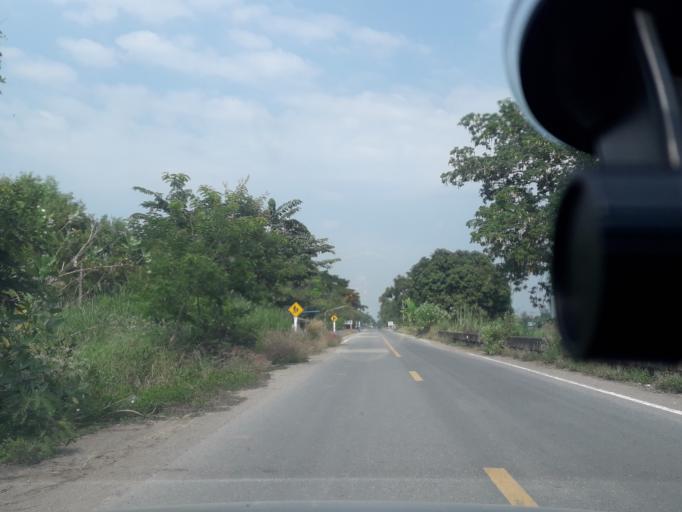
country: TH
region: Pathum Thani
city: Nong Suea
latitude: 14.2182
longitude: 100.8914
